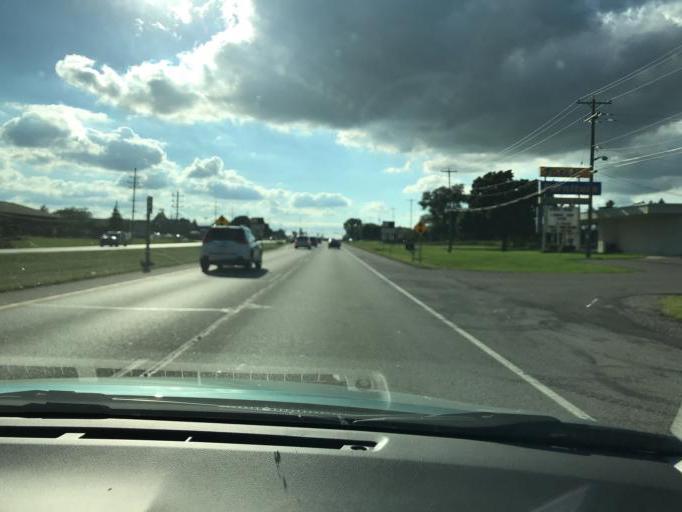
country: US
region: Wisconsin
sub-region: Kenosha County
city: Pleasant Prairie
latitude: 42.5669
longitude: -87.9087
